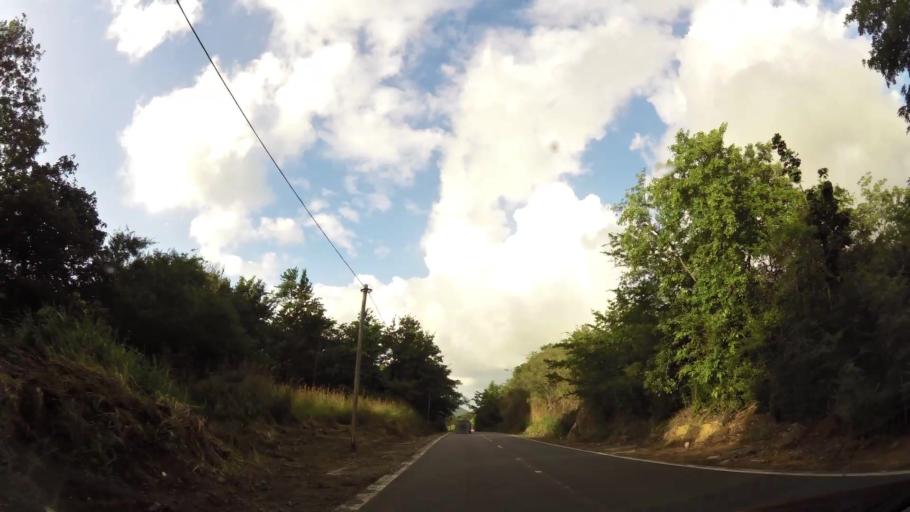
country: DM
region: Saint John
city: Portsmouth
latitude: 15.5411
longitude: -61.4746
